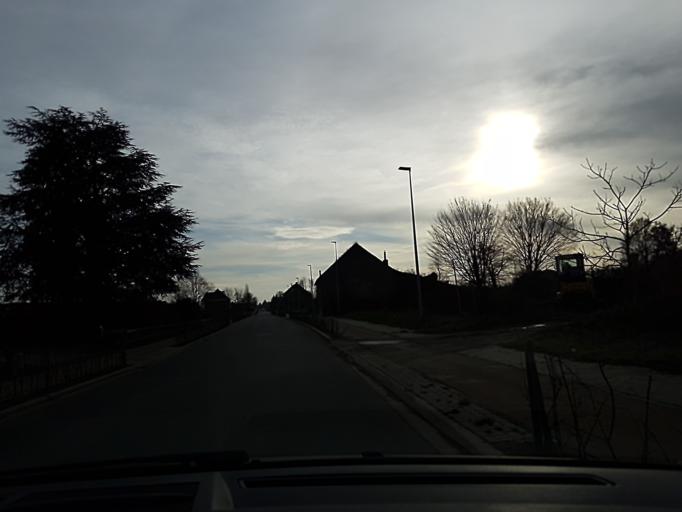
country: BE
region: Flanders
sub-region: Provincie Vlaams-Brabant
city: Herent
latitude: 50.9400
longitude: 4.6835
